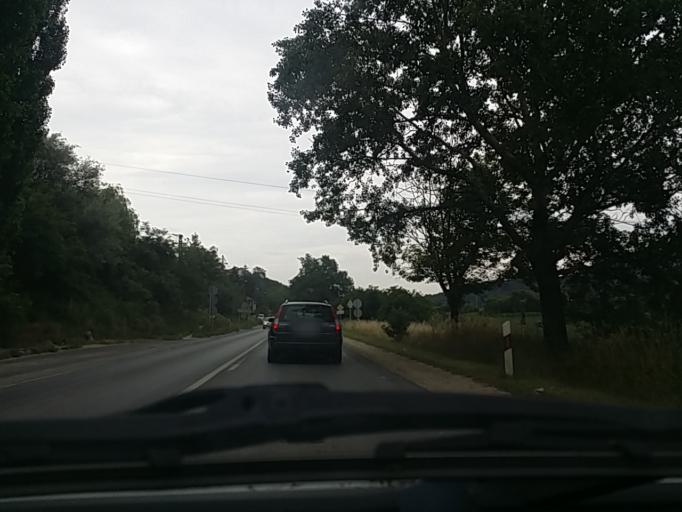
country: HU
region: Pest
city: Pilisborosjeno
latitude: 47.5927
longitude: 18.9833
